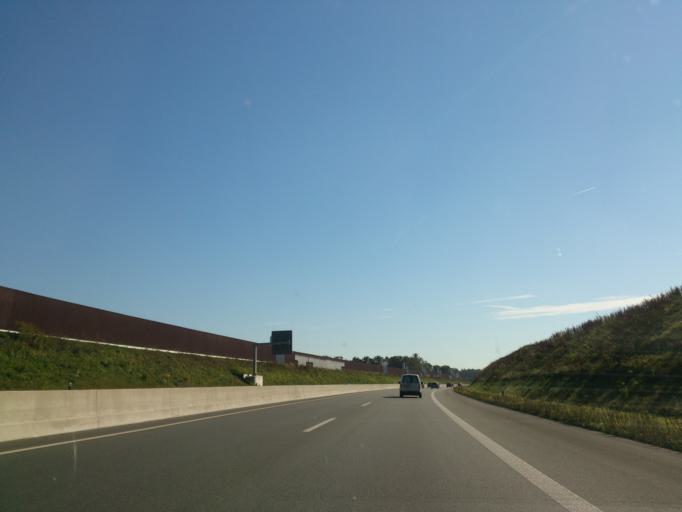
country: DE
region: North Rhine-Westphalia
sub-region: Regierungsbezirk Detmold
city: Bielefeld
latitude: 51.9651
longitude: 8.4979
